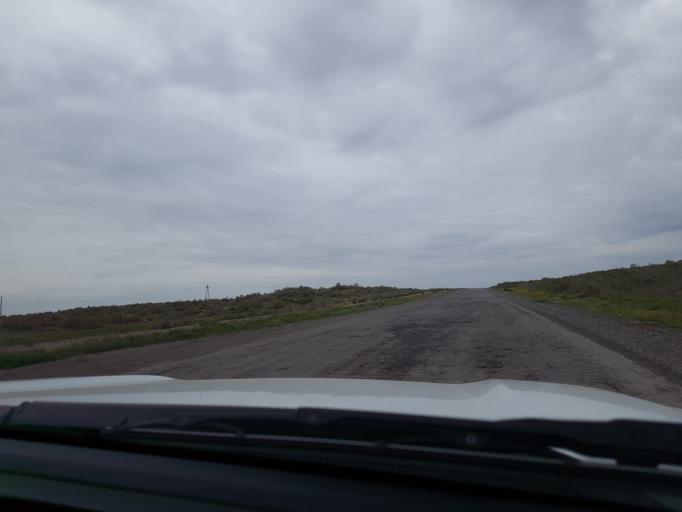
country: TM
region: Mary
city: Bayramaly
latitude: 37.9147
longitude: 62.6219
